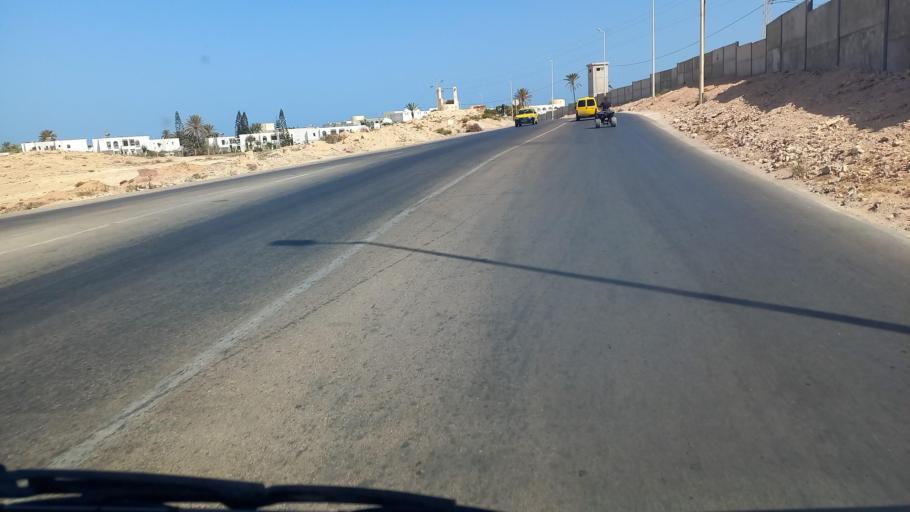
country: TN
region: Madanin
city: Midoun
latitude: 33.8220
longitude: 11.0420
